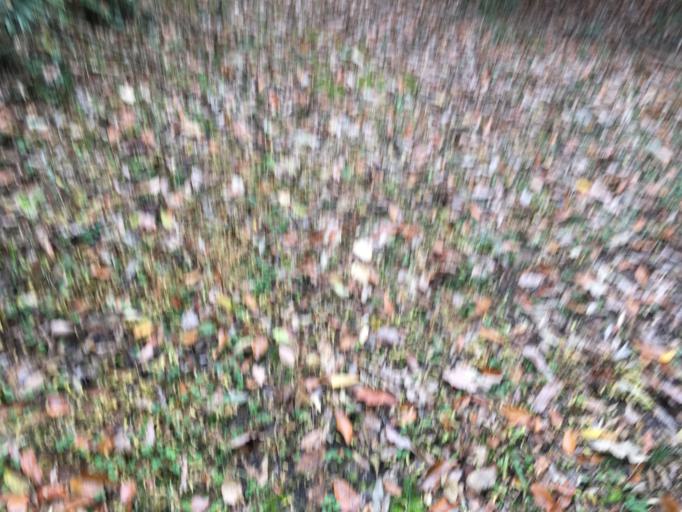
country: JP
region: Kyoto
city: Kameoka
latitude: 34.9872
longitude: 135.5534
